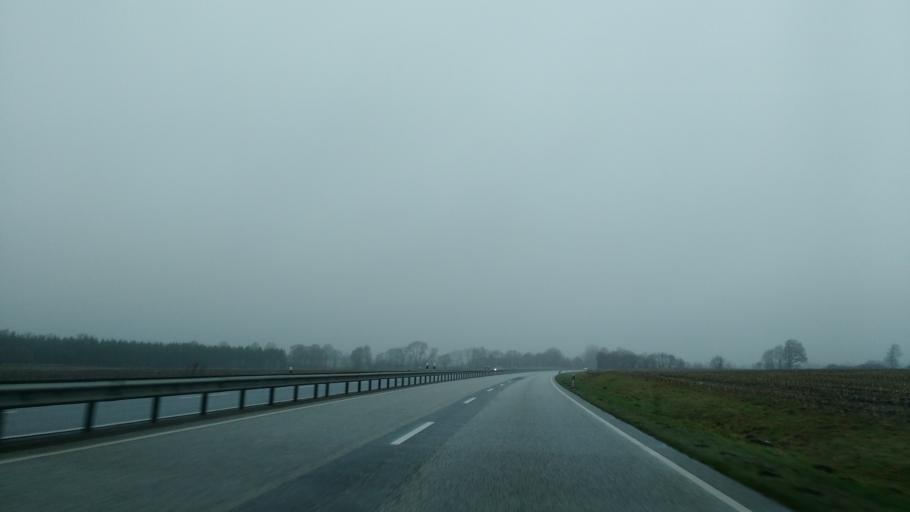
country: DE
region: Schleswig-Holstein
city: Jevenstedt
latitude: 54.2446
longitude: 9.6714
